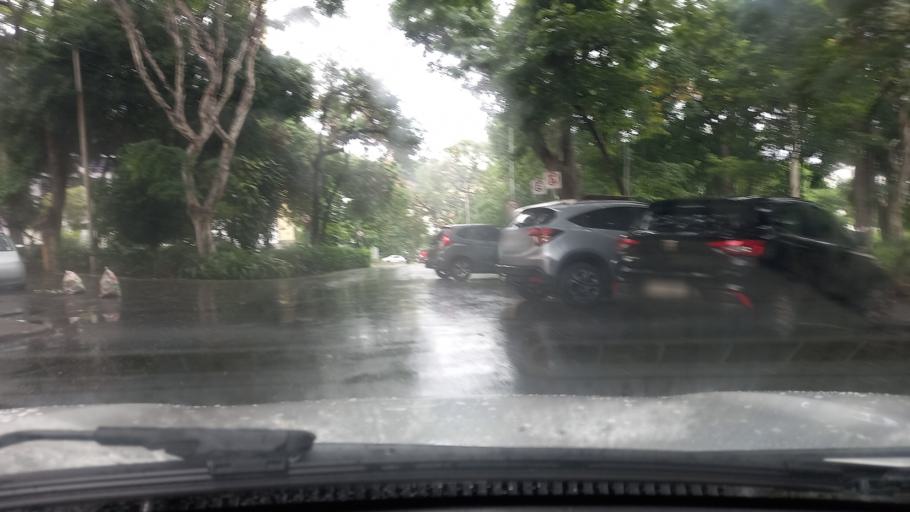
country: BR
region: Minas Gerais
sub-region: Belo Horizonte
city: Belo Horizonte
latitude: -19.9033
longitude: -43.9469
